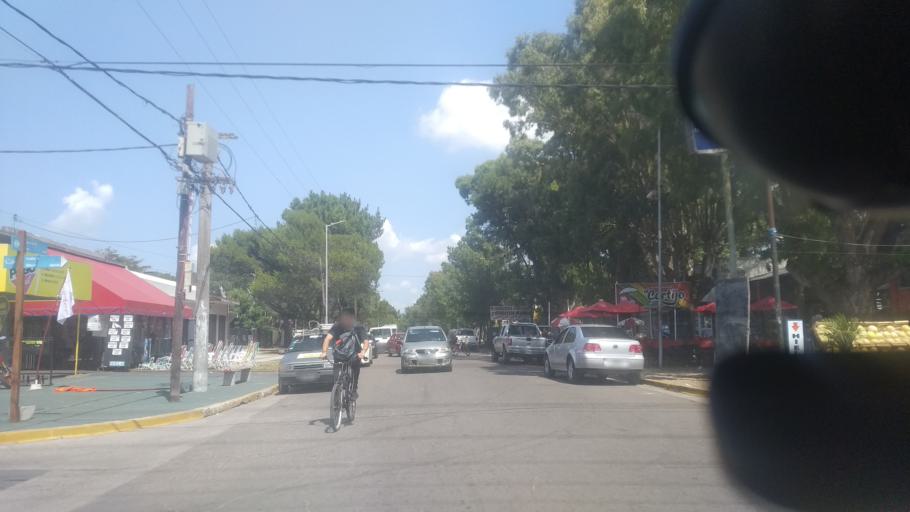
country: AR
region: Buenos Aires
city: Mar del Tuyu
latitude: -36.5591
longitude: -56.6929
